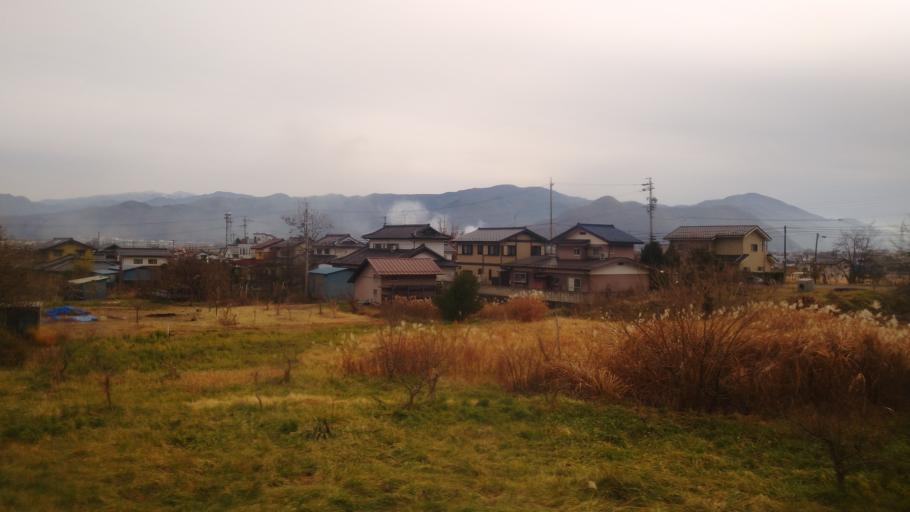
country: JP
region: Nagano
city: Nagano-shi
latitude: 36.5465
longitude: 138.1017
